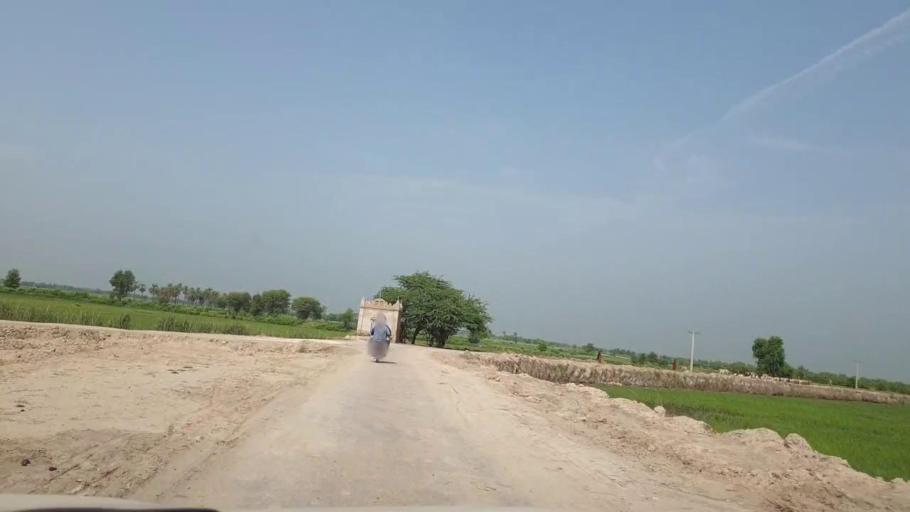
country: PK
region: Sindh
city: Dokri
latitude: 27.4300
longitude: 68.2052
